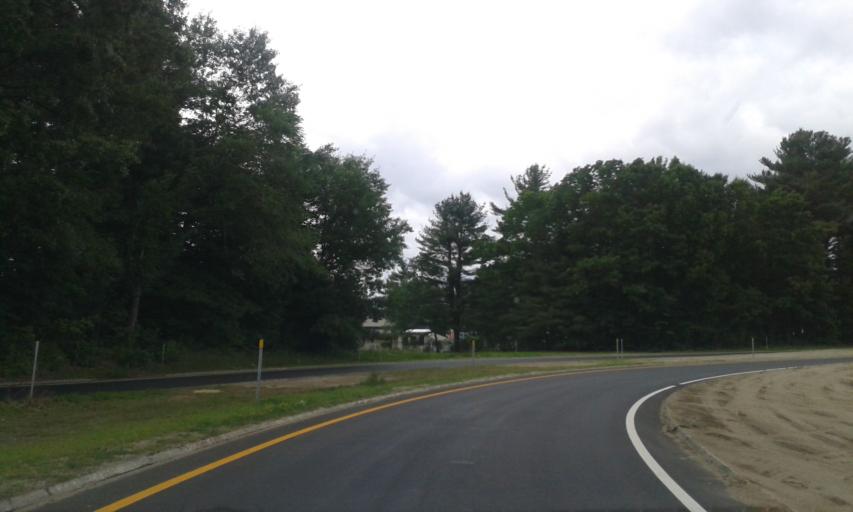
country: US
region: New Hampshire
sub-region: Merrimack County
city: Concord
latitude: 43.1795
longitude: -71.5330
